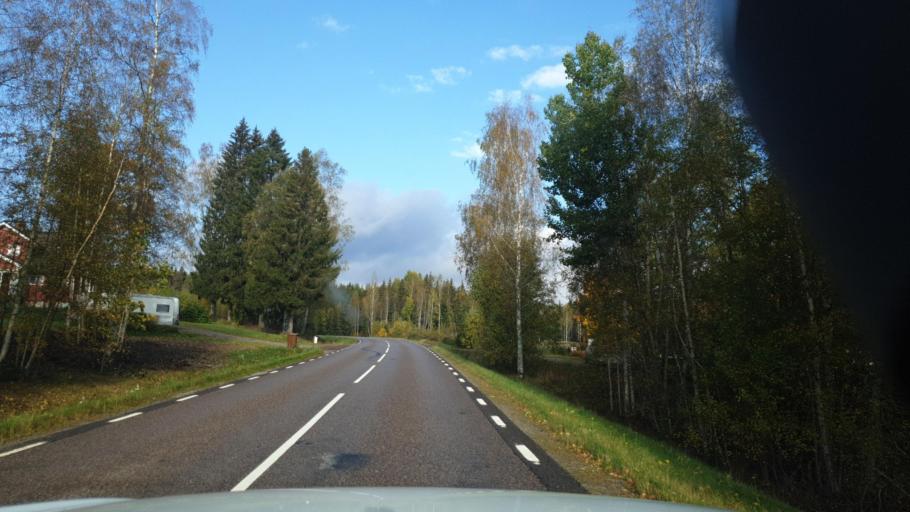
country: SE
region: Vaermland
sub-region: Arvika Kommun
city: Arvika
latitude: 59.5024
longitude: 12.6807
